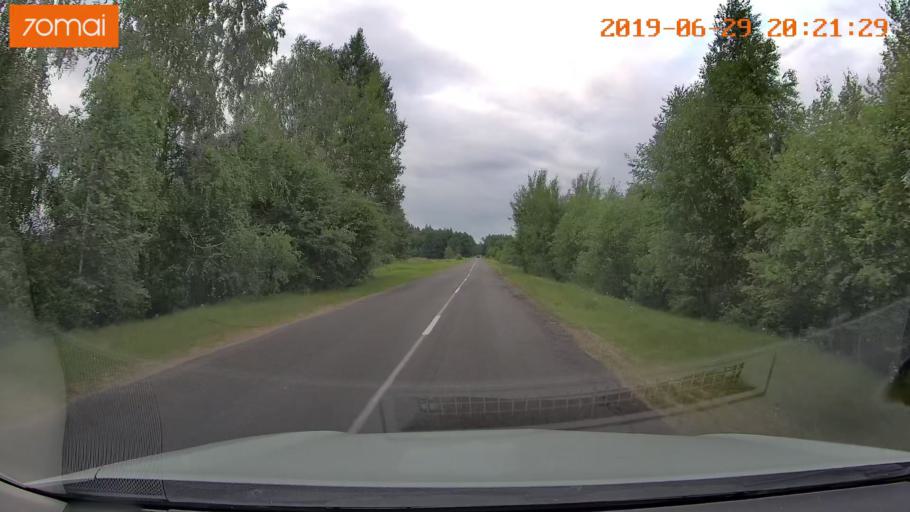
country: BY
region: Brest
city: Asnyezhytsy
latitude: 52.4202
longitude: 26.2530
